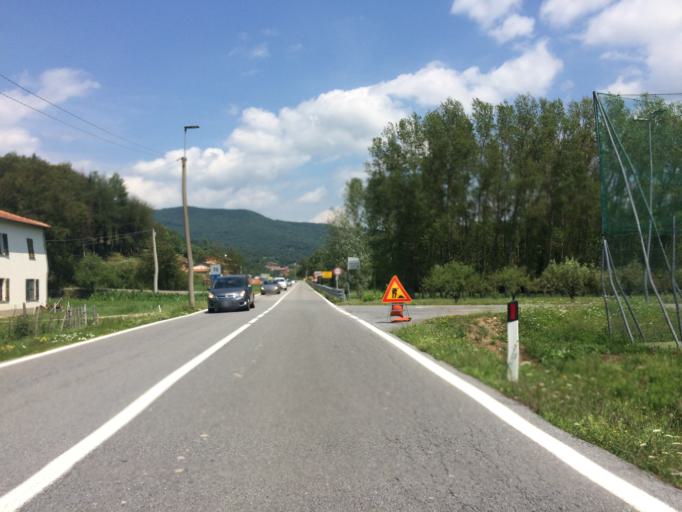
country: IT
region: Piedmont
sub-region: Provincia di Cuneo
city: Priola
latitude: 44.2485
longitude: 8.0216
